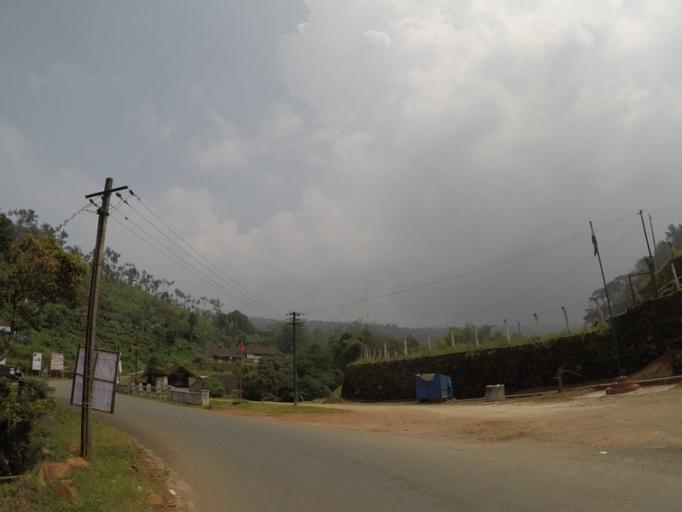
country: IN
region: Karnataka
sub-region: Chikmagalur
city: Mudigere
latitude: 13.1642
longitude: 75.4567
